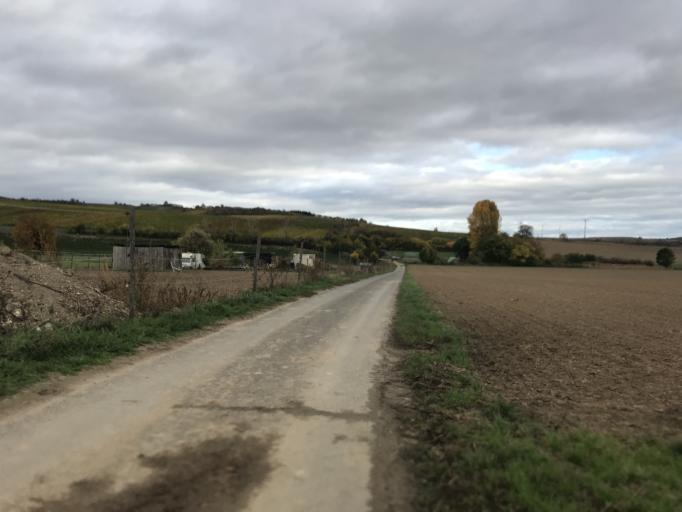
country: DE
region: Rheinland-Pfalz
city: Essenheim
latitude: 49.9258
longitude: 8.1687
